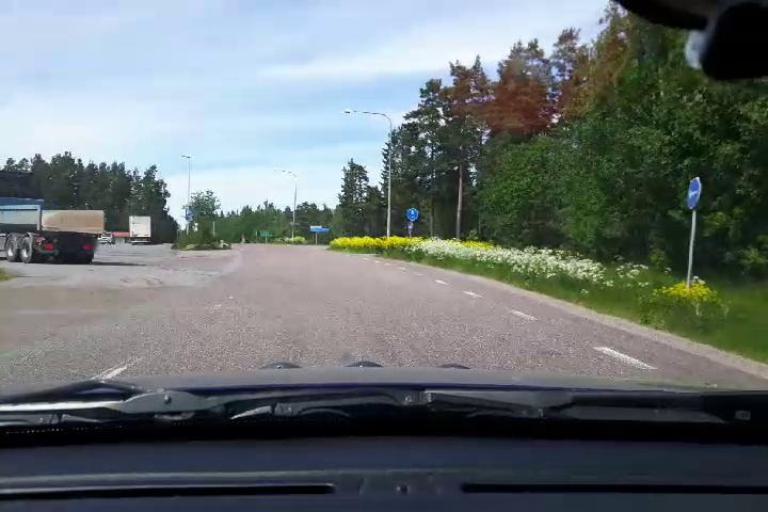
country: SE
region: Gaevleborg
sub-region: Gavle Kommun
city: Gavle
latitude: 60.6490
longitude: 17.1212
